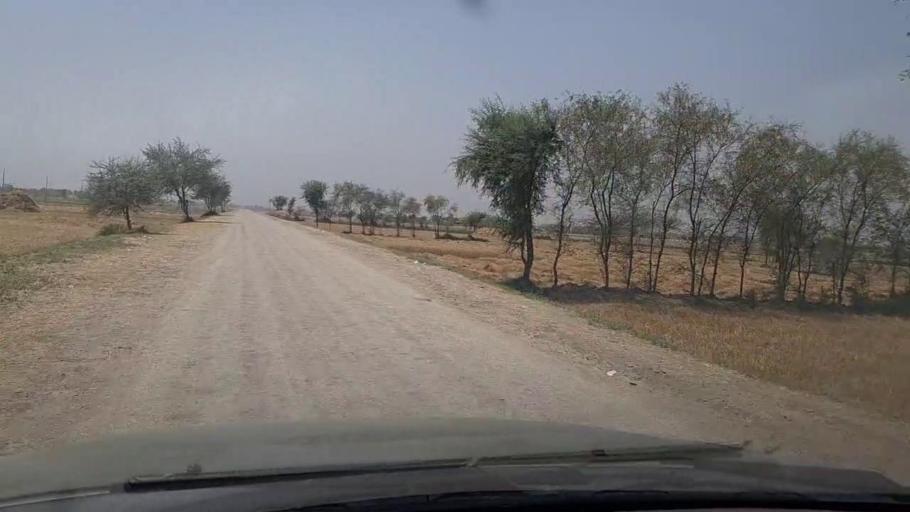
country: PK
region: Sindh
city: Ratodero
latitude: 27.7938
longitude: 68.2394
